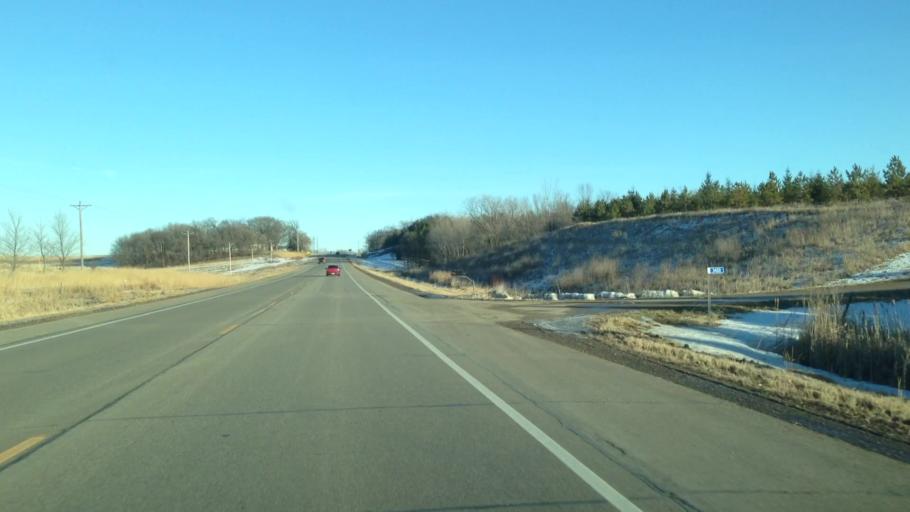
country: US
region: Minnesota
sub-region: Scott County
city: Elko New Market
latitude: 44.4792
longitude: -93.3306
